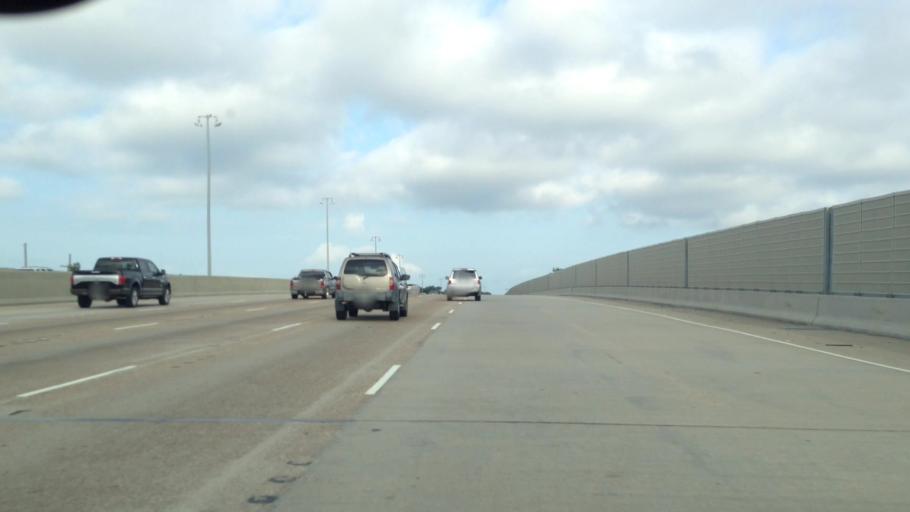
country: US
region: Louisiana
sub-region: Jefferson Parish
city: Metairie Terrace
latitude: 29.9997
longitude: -90.1913
